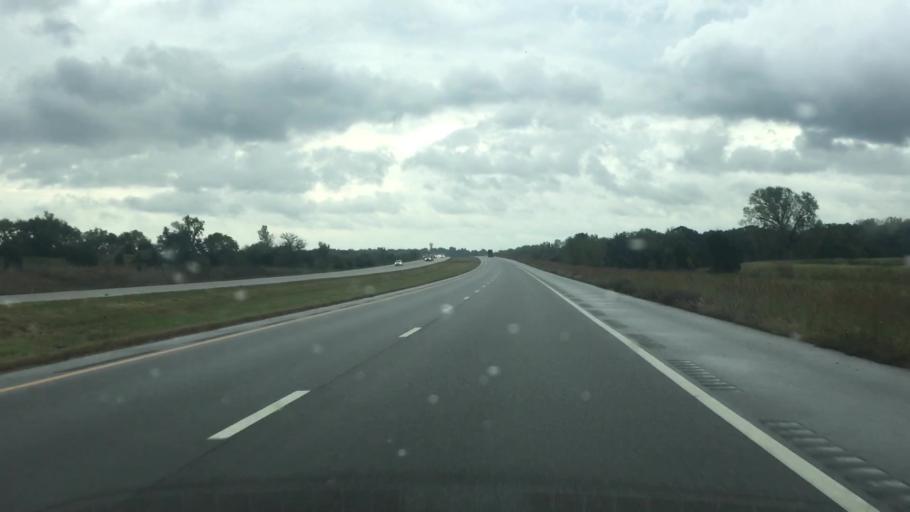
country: US
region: Kansas
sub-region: Miami County
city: Paola
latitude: 38.5467
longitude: -94.8774
